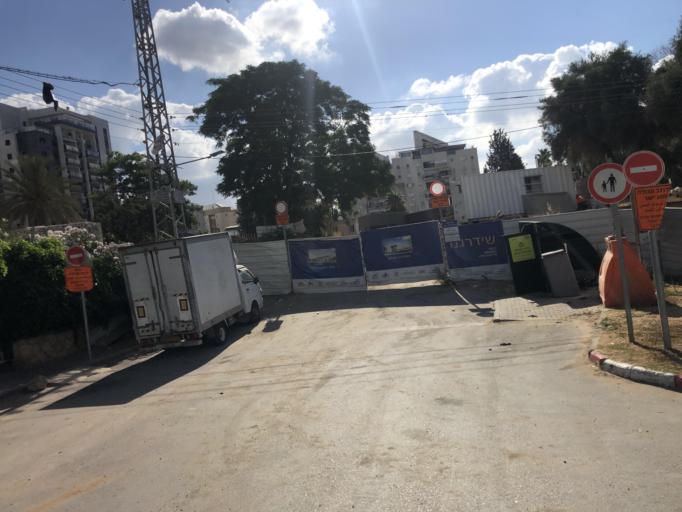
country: IL
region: Central District
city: Yehud
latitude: 32.0314
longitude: 34.8895
